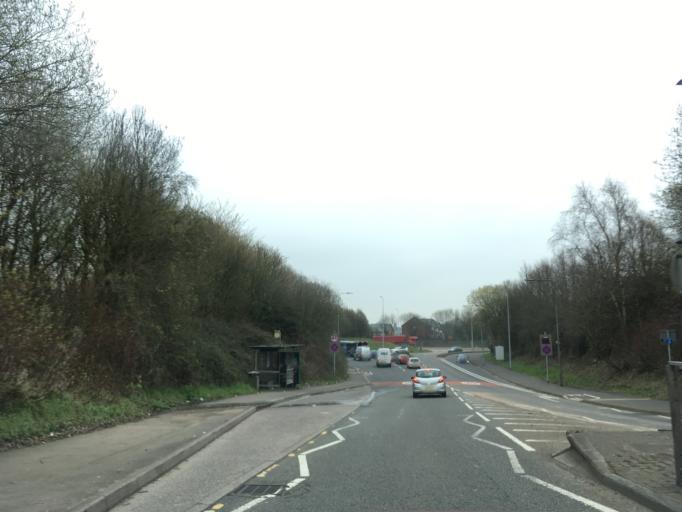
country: GB
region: Wales
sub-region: Newport
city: Marshfield
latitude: 51.5344
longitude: -3.1294
